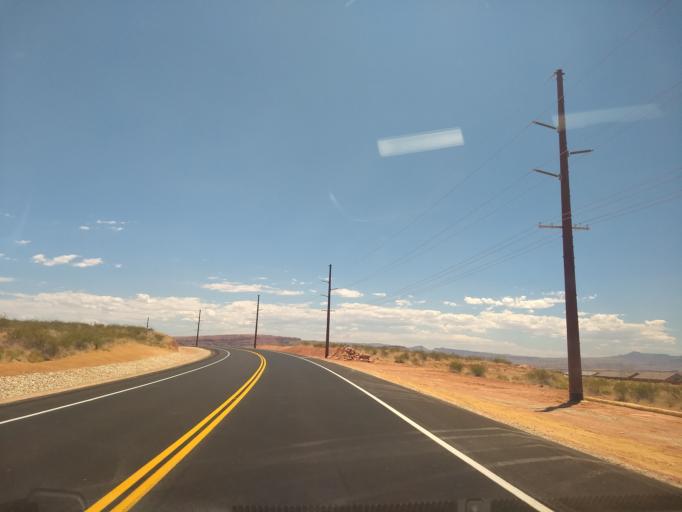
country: US
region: Utah
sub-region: Washington County
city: Washington
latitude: 37.1504
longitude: -113.5164
